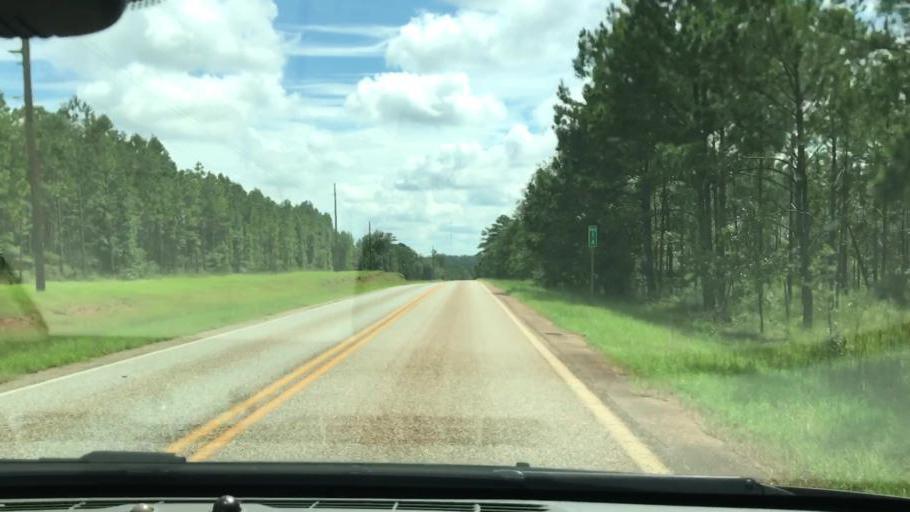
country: US
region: Georgia
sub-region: Stewart County
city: Lumpkin
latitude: 32.0619
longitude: -84.8290
